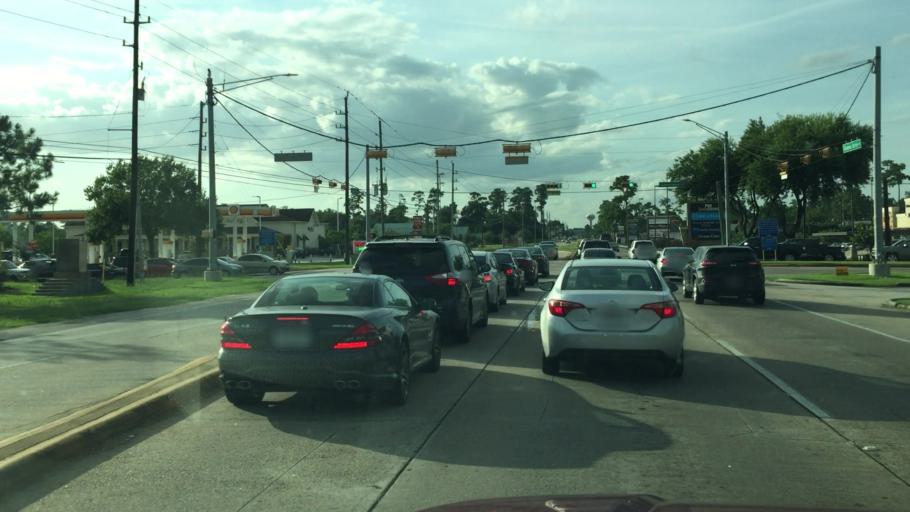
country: US
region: Texas
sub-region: Harris County
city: Hudson
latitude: 30.0102
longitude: -95.5145
